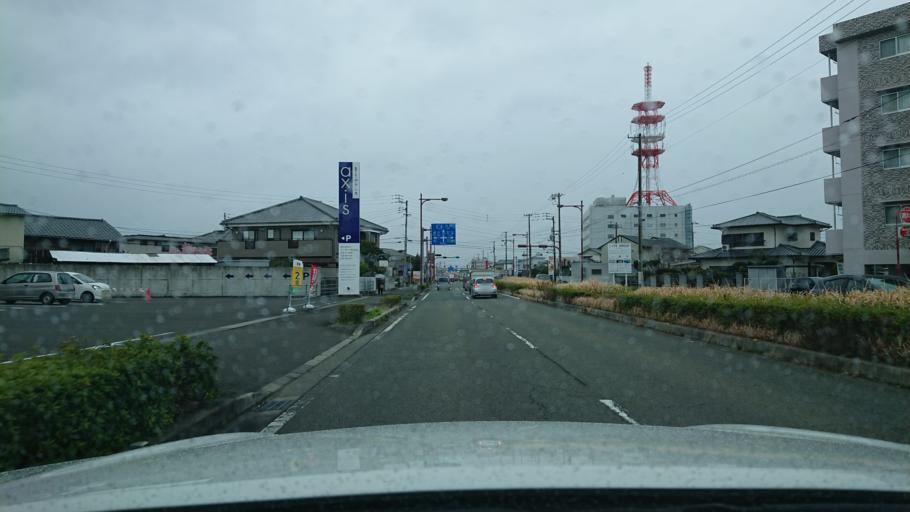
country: JP
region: Tokushima
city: Tokushima-shi
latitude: 34.0833
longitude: 134.5164
